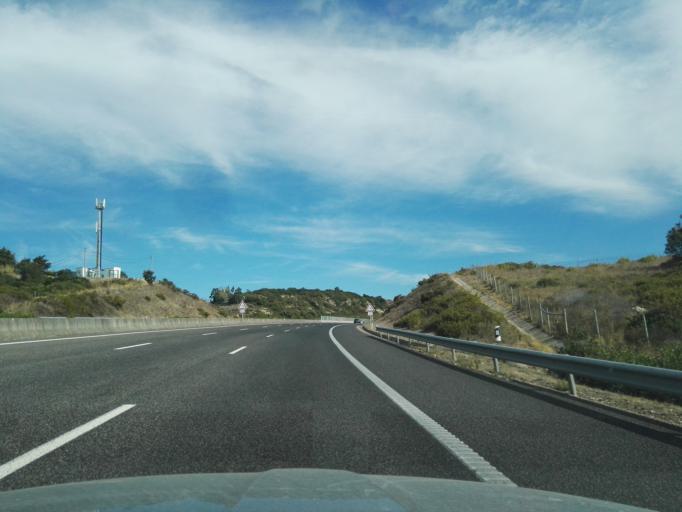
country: PT
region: Lisbon
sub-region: Loures
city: Bucelas
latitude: 38.9223
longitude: -9.0756
